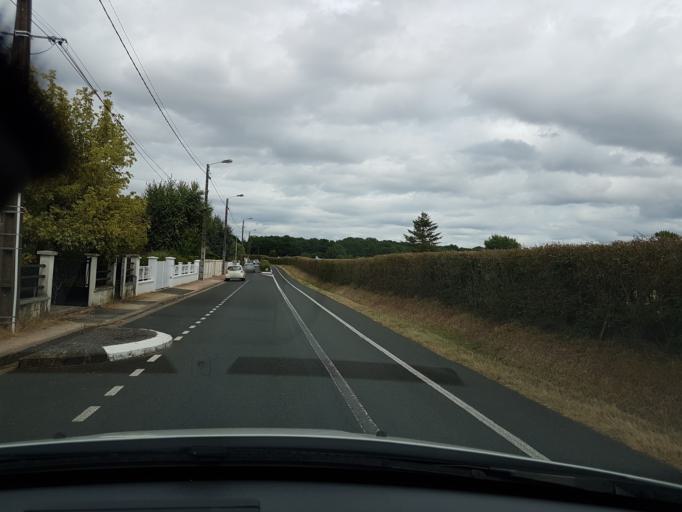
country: FR
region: Centre
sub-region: Departement d'Indre-et-Loire
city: Chambray-les-Tours
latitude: 47.3318
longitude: 0.7105
